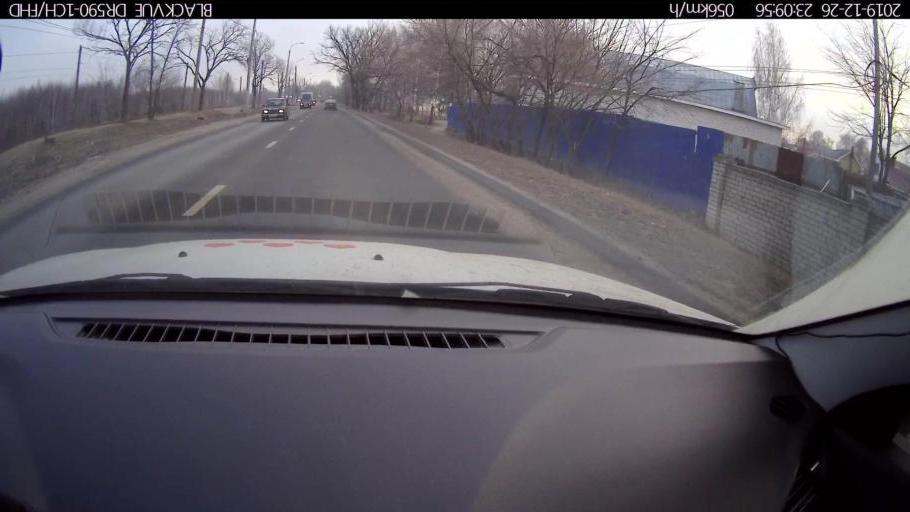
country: RU
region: Nizjnij Novgorod
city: Gorbatovka
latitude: 56.2059
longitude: 43.7740
